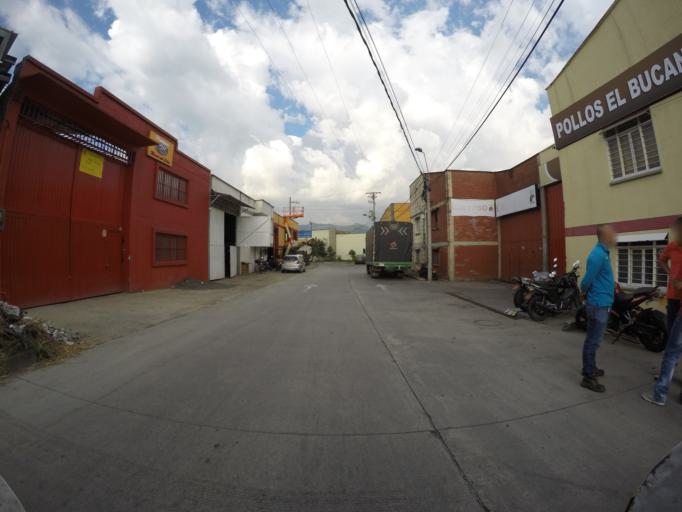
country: CO
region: Risaralda
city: Pereira
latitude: 4.8241
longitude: -75.6886
